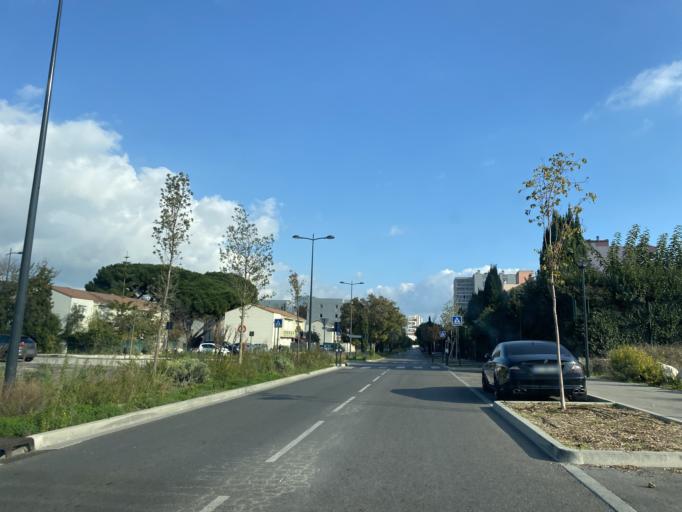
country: FR
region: Provence-Alpes-Cote d'Azur
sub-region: Departement du Var
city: Six-Fours-les-Plages
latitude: 43.1102
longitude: 5.8645
